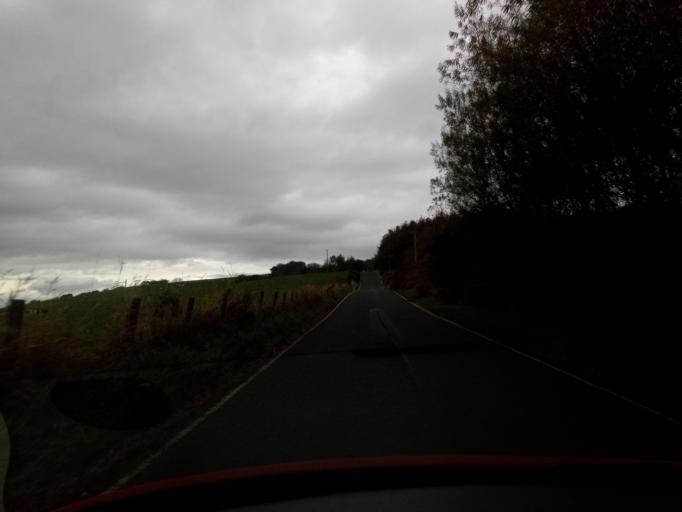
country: GB
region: Scotland
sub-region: West Lothian
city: Bathgate
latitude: 55.9220
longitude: -3.6356
